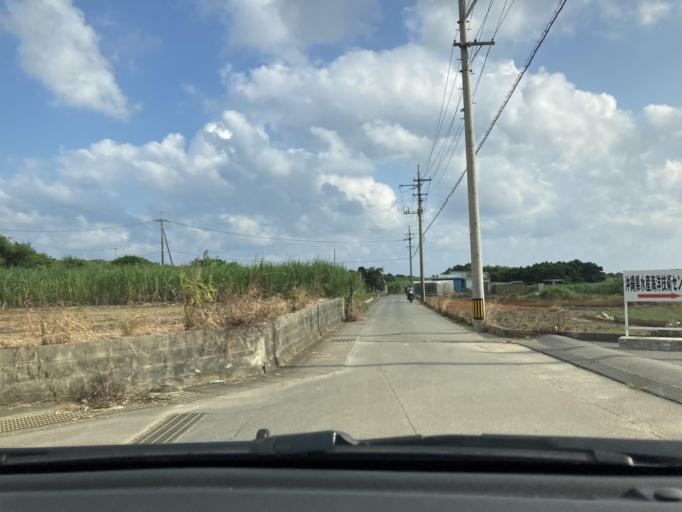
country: JP
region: Okinawa
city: Itoman
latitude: 26.0863
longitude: 127.6624
